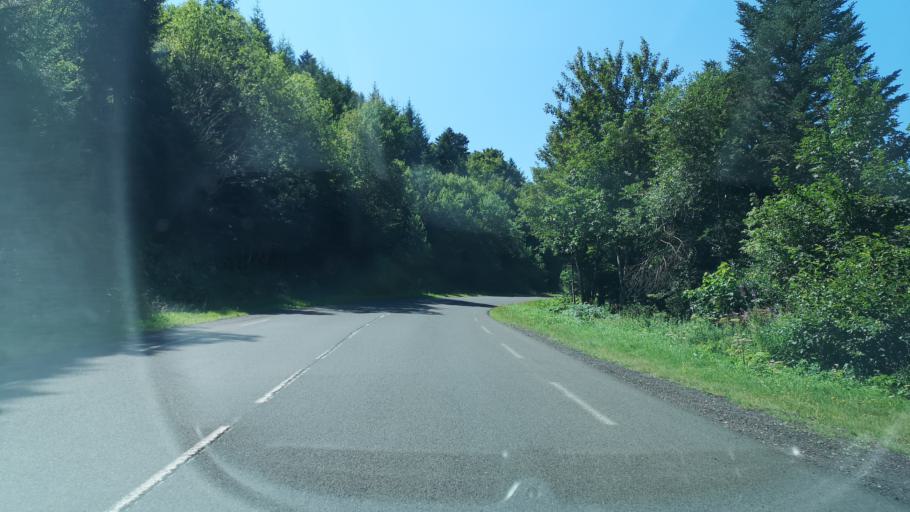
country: FR
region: Auvergne
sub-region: Departement du Puy-de-Dome
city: Mont-Dore
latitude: 45.5938
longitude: 2.8264
